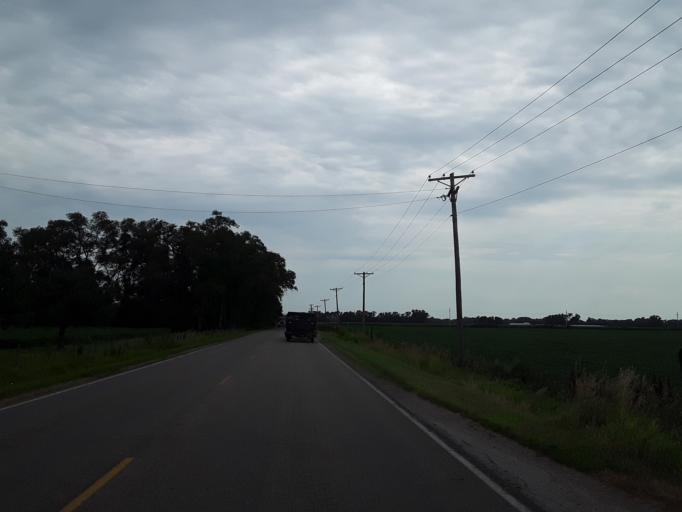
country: US
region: Nebraska
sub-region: Douglas County
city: Valley
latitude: 41.2521
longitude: -96.3305
